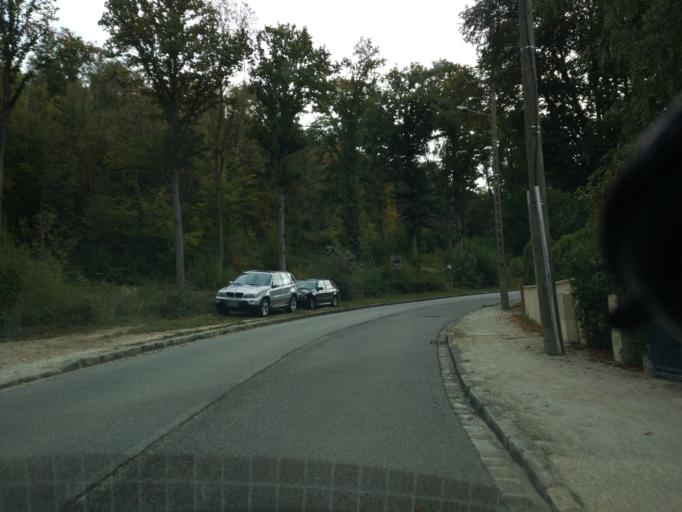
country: FR
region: Ile-de-France
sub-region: Departement des Yvelines
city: Saint-Remy-les-Chevreuse
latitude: 48.6958
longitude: 2.0673
